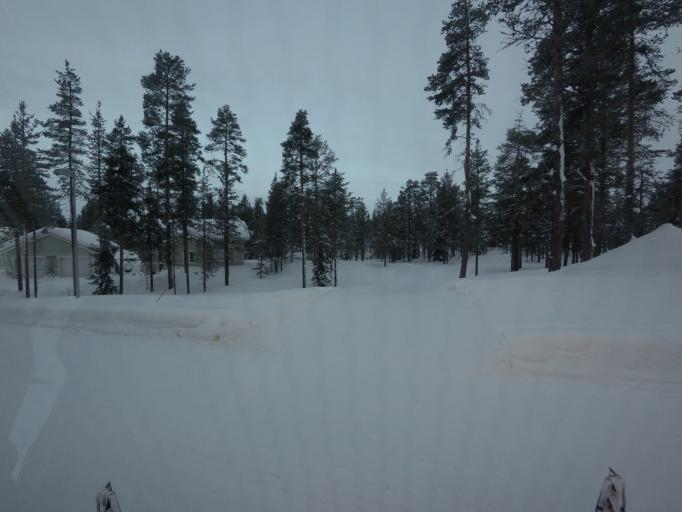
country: FI
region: Lapland
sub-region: Tunturi-Lappi
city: Kolari
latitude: 67.6220
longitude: 24.1488
